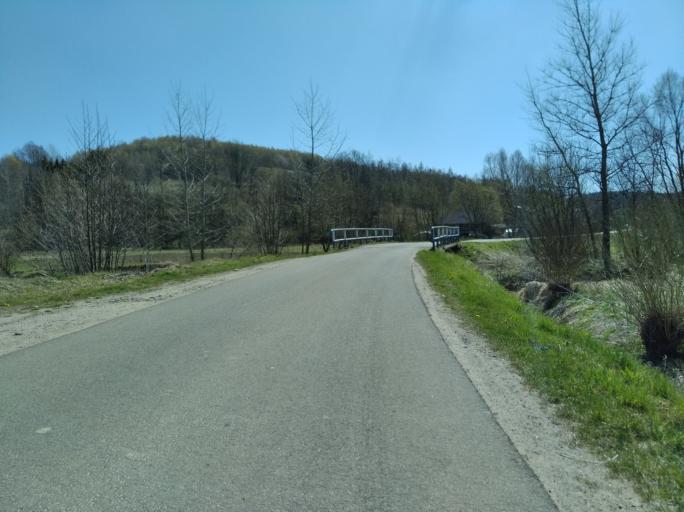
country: PL
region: Subcarpathian Voivodeship
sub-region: Powiat brzozowski
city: Jablonka
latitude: 49.7355
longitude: 22.1435
